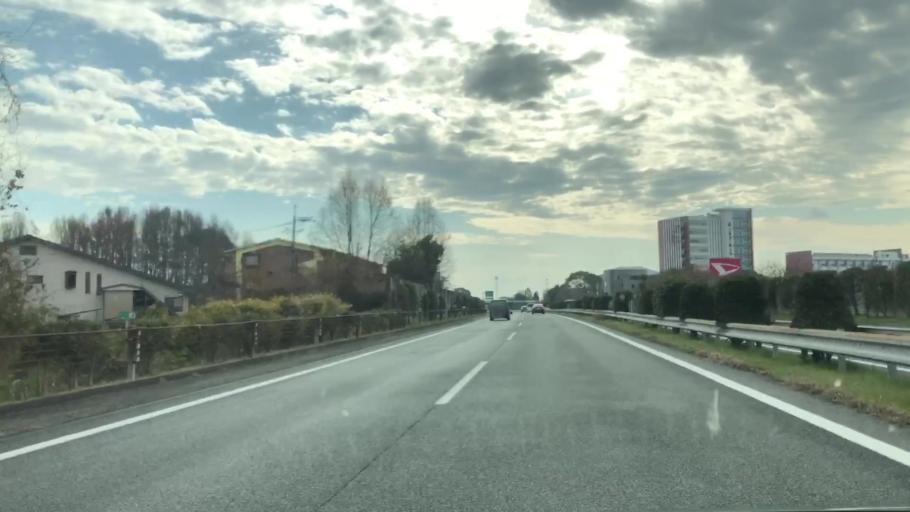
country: JP
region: Fukuoka
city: Kurume
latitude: 33.2688
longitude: 130.5396
